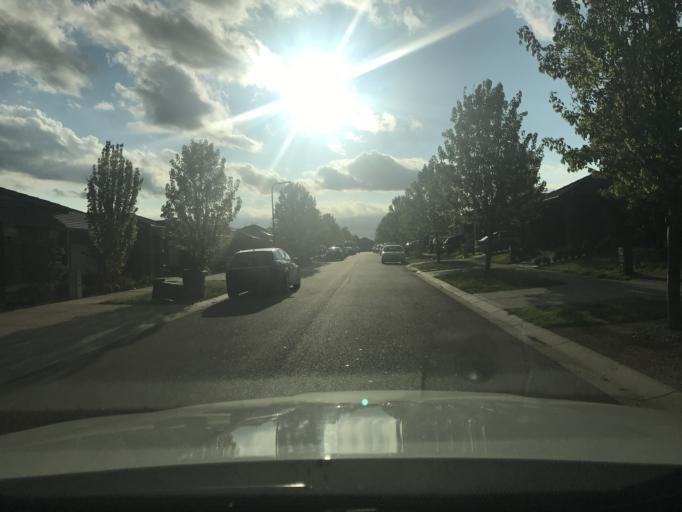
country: AU
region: Victoria
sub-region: Hume
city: Craigieburn
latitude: -37.5739
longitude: 144.9054
